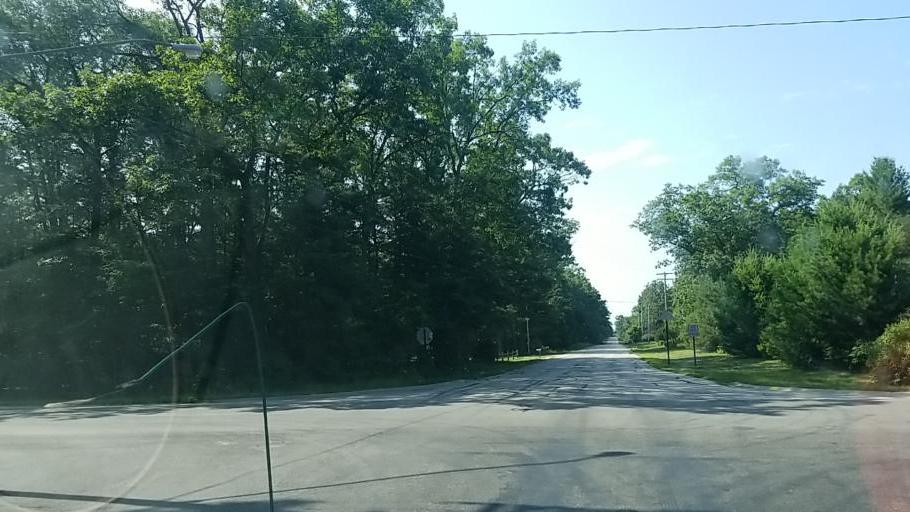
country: US
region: Michigan
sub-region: Muskegon County
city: Whitehall
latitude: 43.3348
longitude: -86.3767
